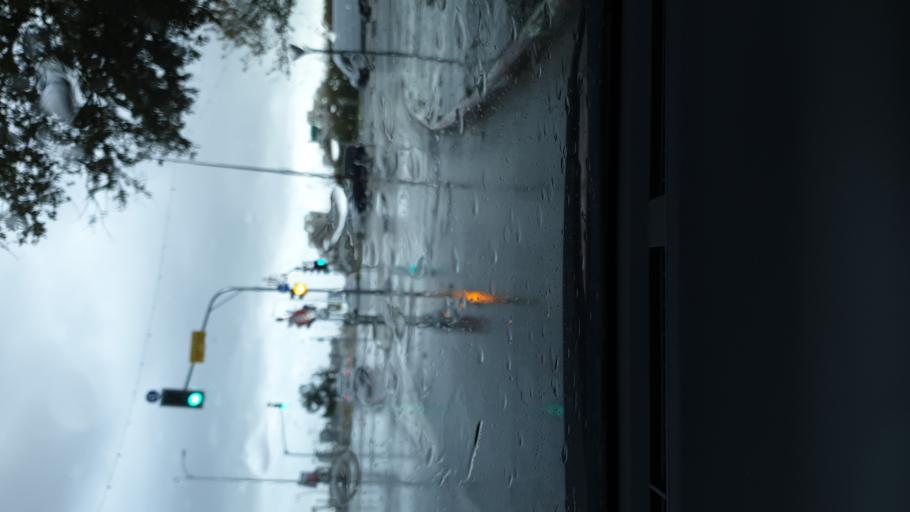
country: IL
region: Central District
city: Modiin
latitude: 31.8939
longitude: 35.0018
